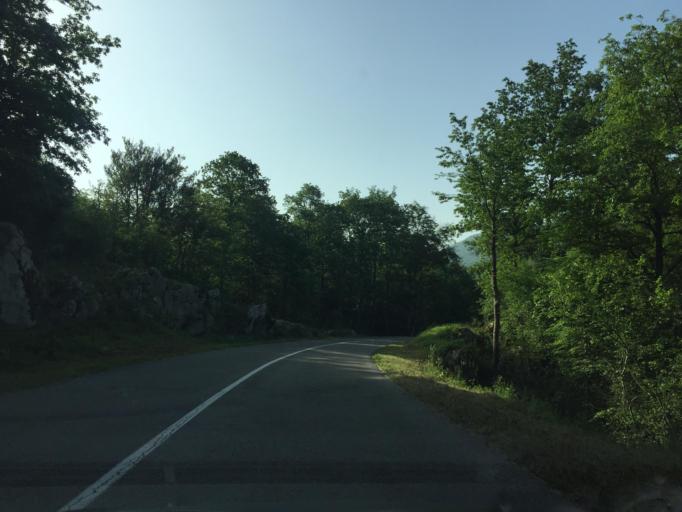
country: HR
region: Primorsko-Goranska
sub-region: Grad Opatija
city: Opatija
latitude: 45.4318
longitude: 14.2020
